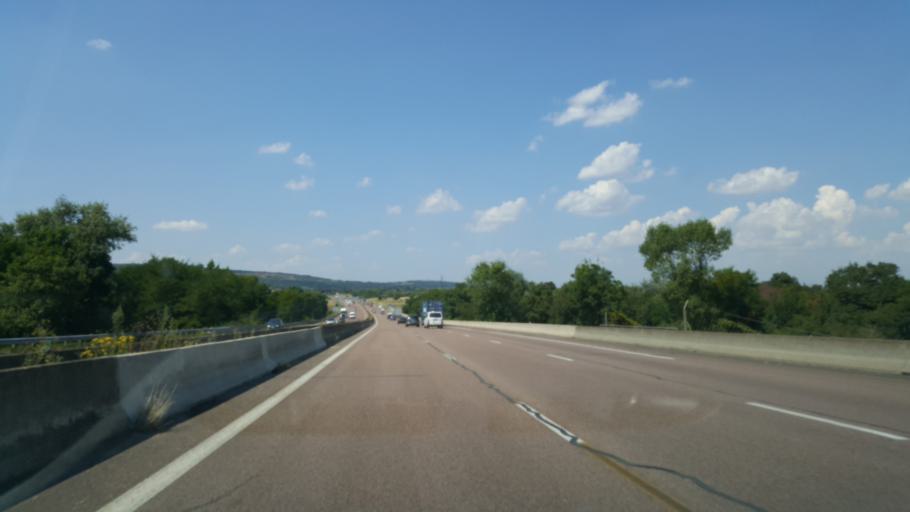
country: FR
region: Bourgogne
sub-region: Departement de Saone-et-Loire
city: Tournus
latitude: 46.5961
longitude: 4.8937
